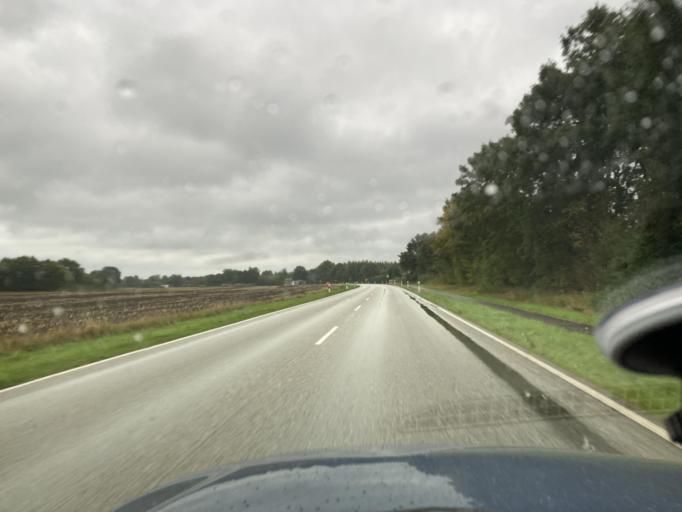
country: DE
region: Schleswig-Holstein
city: Hamdorf
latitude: 54.2502
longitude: 9.5317
